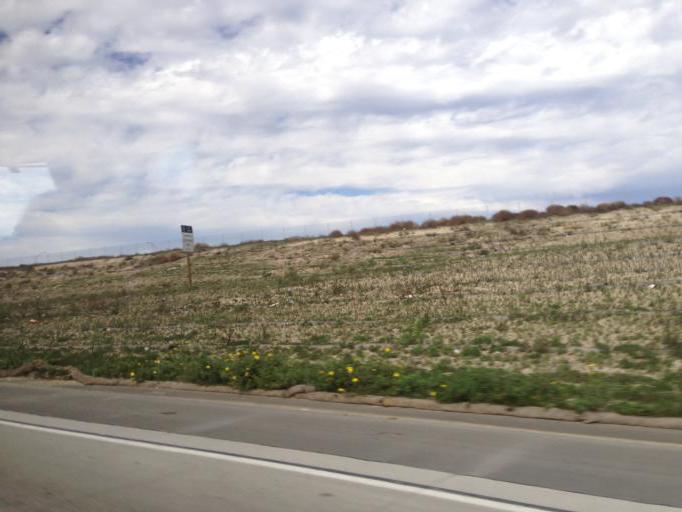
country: MX
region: Baja California
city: Tijuana
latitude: 32.5667
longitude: -117.0156
